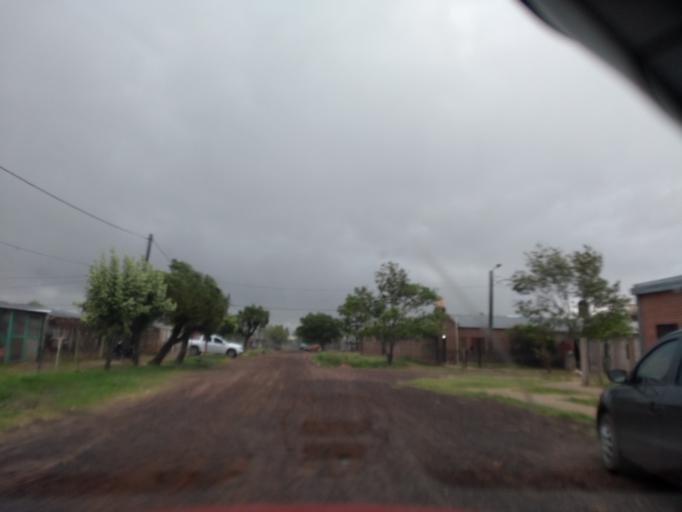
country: AR
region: Chaco
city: Fontana
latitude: -27.4199
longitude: -59.0487
